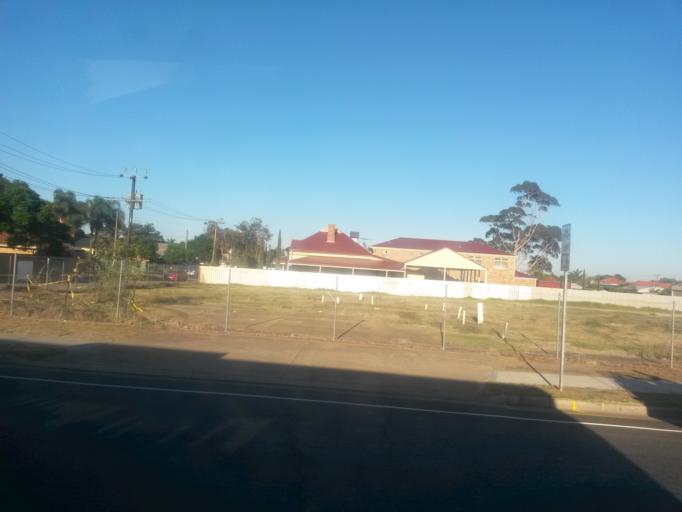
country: AU
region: South Australia
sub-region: Port Adelaide Enfield
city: Alberton
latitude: -34.8576
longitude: 138.5292
